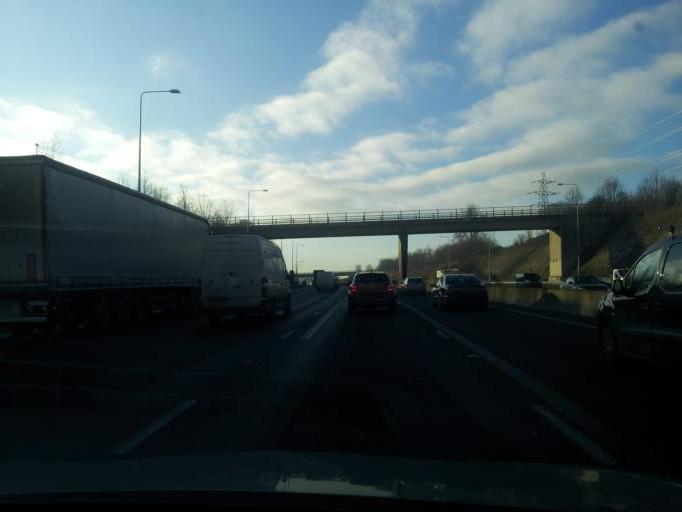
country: GB
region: England
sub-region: Buckinghamshire
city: Chalfont Saint Peter
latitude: 51.6240
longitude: -0.5238
